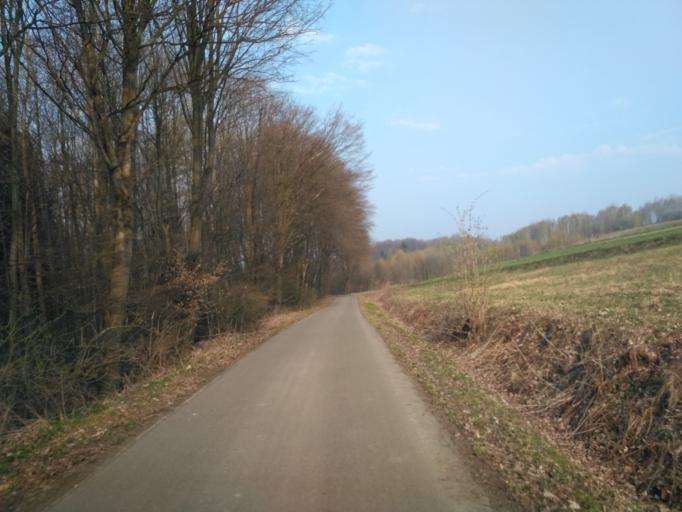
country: PL
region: Subcarpathian Voivodeship
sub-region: Powiat strzyzowski
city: Wisniowa
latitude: 49.8859
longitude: 21.6322
